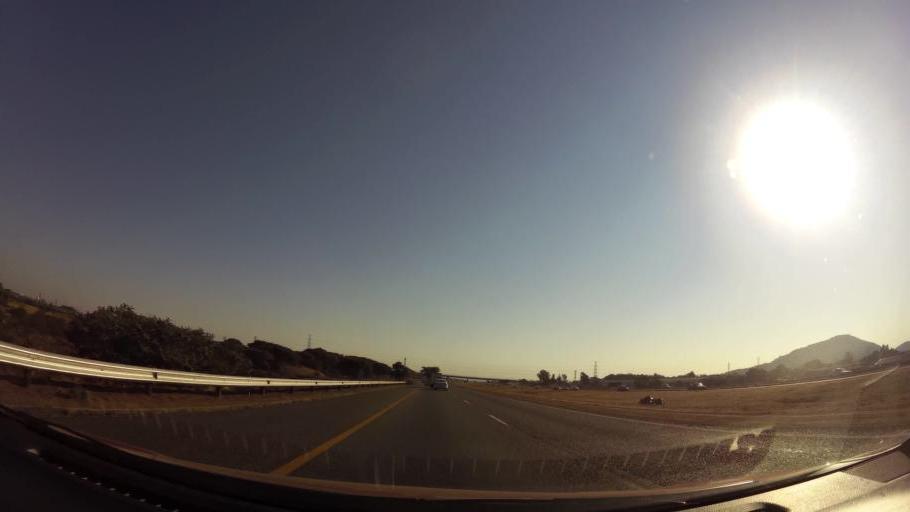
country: ZA
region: North-West
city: Ga-Rankuwa
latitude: -25.6359
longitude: 28.1111
